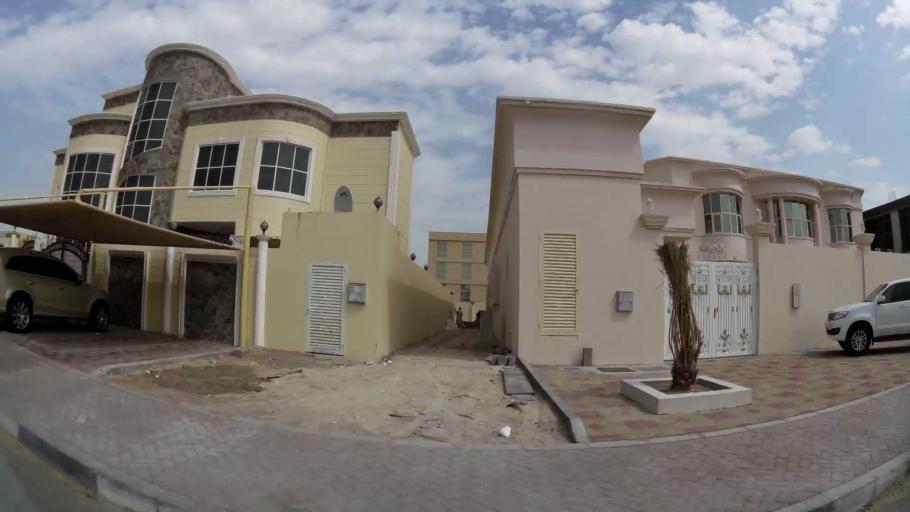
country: AE
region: Abu Dhabi
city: Abu Dhabi
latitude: 24.3040
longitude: 54.6189
